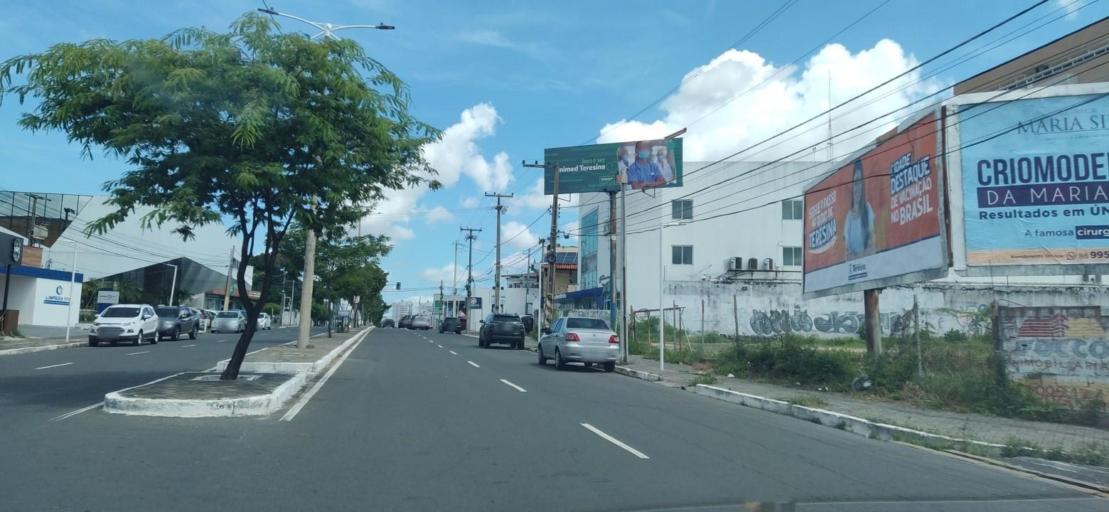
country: BR
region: Piaui
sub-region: Teresina
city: Teresina
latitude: -5.0663
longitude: -42.7935
